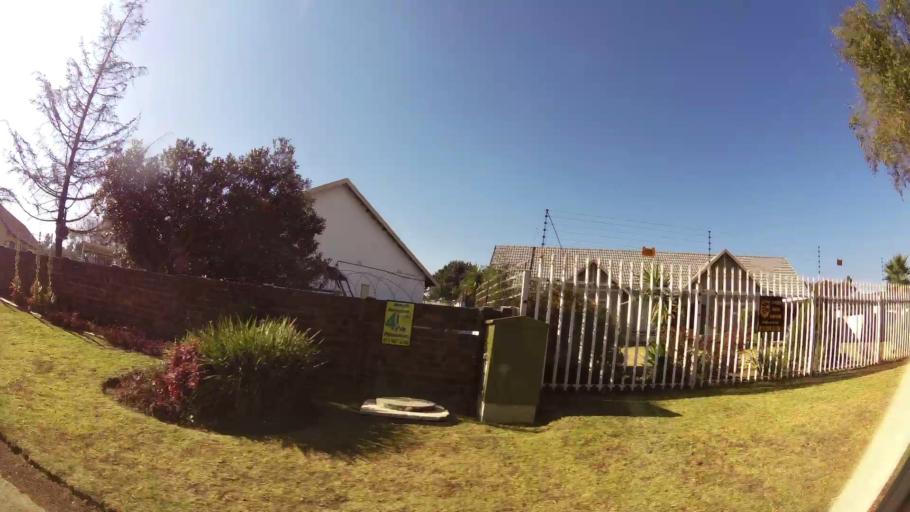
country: ZA
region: Gauteng
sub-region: Ekurhuleni Metropolitan Municipality
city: Germiston
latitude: -26.3428
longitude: 28.1034
